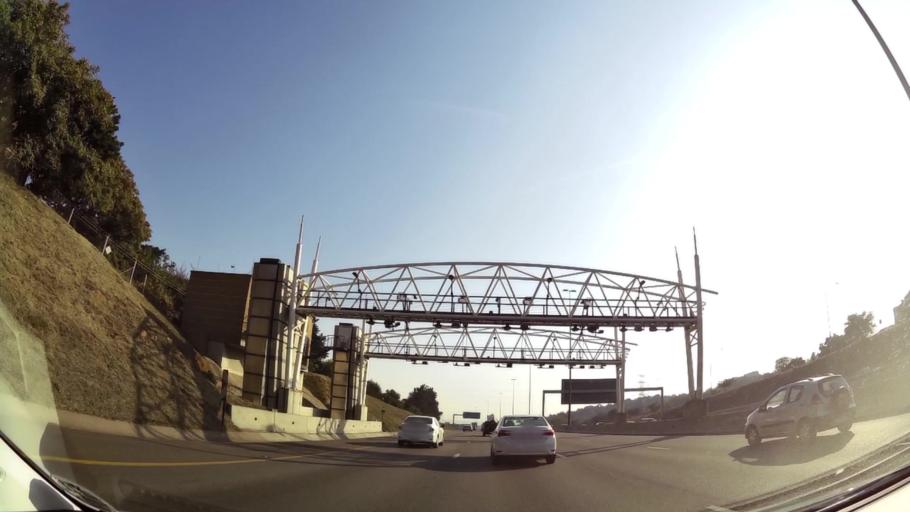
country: ZA
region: Gauteng
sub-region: City of Tshwane Metropolitan Municipality
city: Pretoria
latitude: -25.7562
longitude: 28.2746
